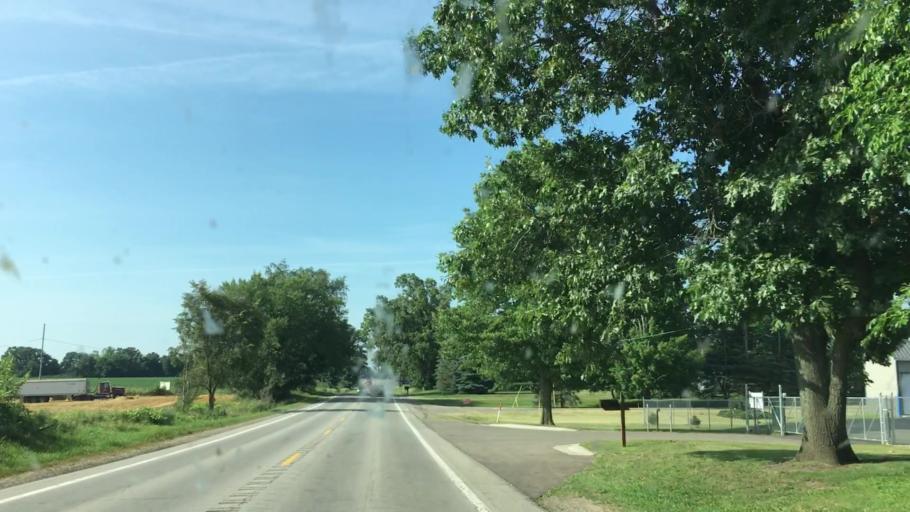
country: US
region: Michigan
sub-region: Kalamazoo County
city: South Gull Lake
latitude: 42.3958
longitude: -85.4552
